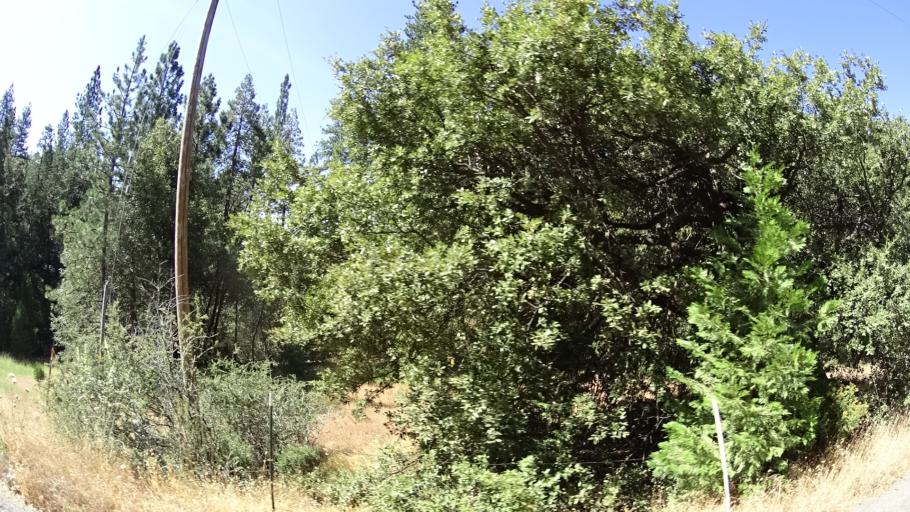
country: US
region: California
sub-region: Amador County
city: Pioneer
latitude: 38.3959
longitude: -120.4804
